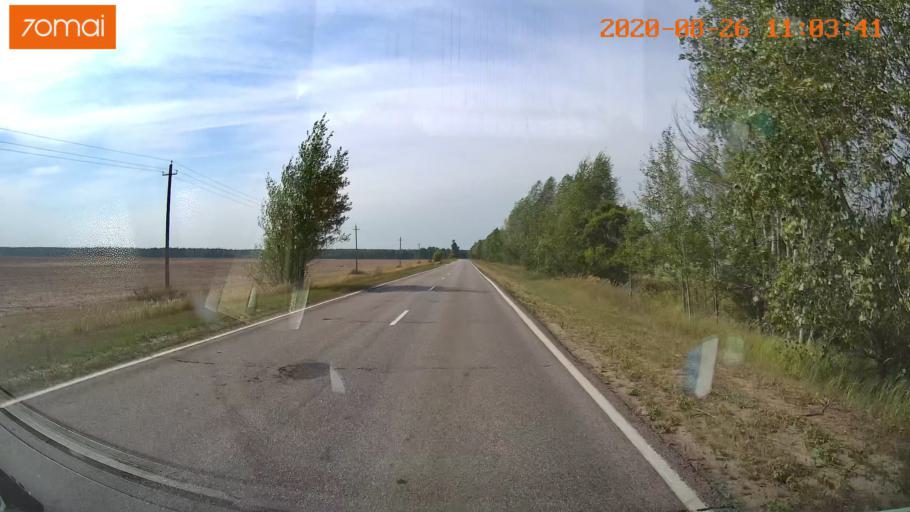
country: RU
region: Rjazan
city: Izhevskoye
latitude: 54.5384
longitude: 41.2081
